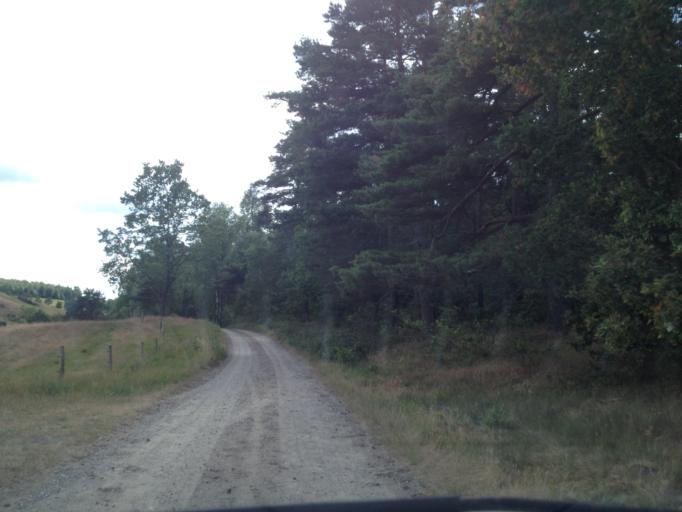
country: DK
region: Central Jutland
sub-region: Syddjurs Kommune
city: Ronde
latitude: 56.2149
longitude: 10.5290
